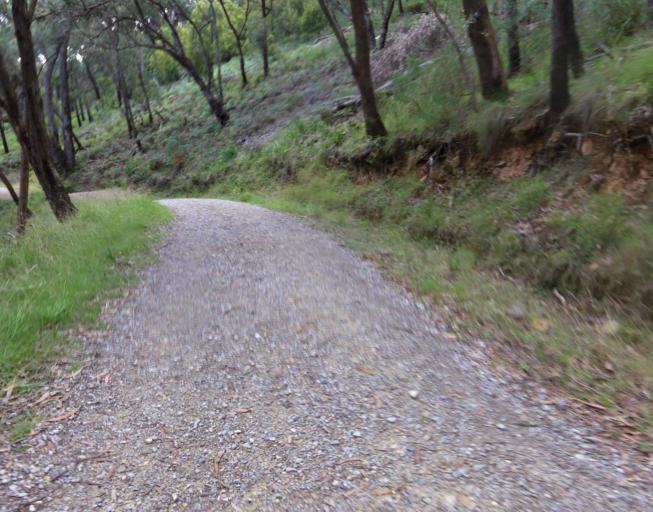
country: AU
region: Victoria
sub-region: Yarra Ranges
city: Montrose
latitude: -37.8339
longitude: 145.3435
